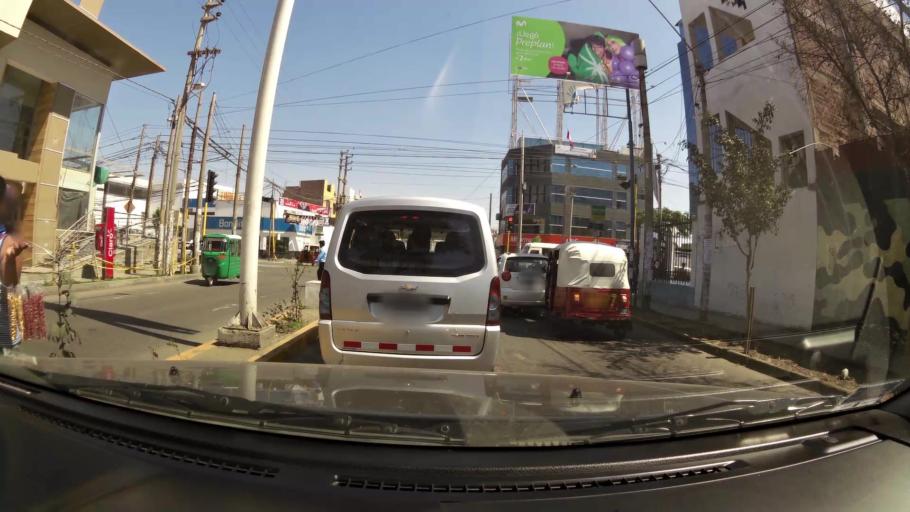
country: PE
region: Ica
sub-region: Provincia de Ica
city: Ica
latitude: -14.0720
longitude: -75.7278
